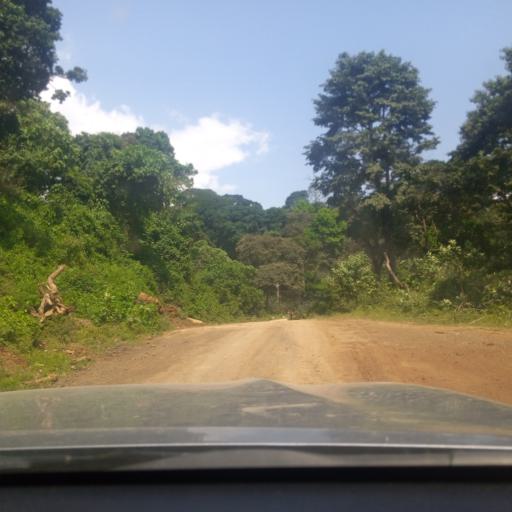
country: ET
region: Southern Nations, Nationalities, and People's Region
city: Tippi
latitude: 7.0710
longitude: 35.4337
